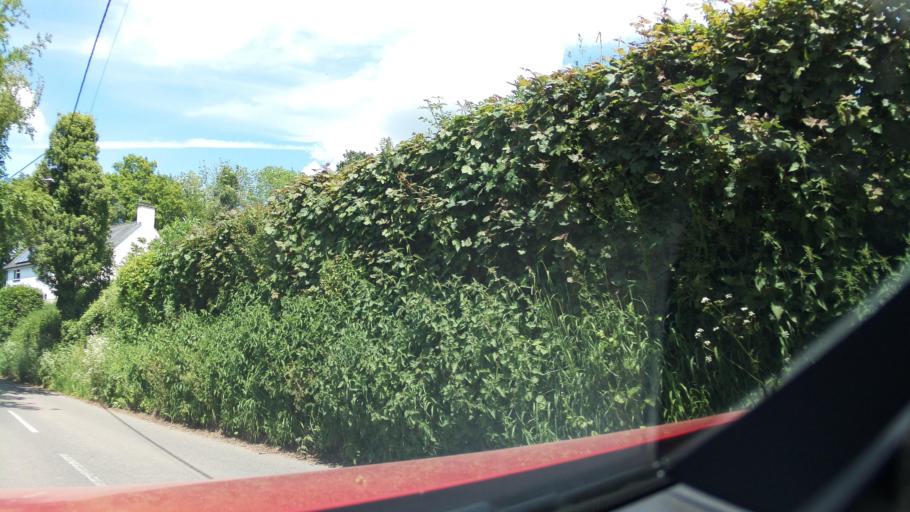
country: GB
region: Wales
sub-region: Monmouthshire
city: Monmouth
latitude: 51.8275
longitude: -2.7500
